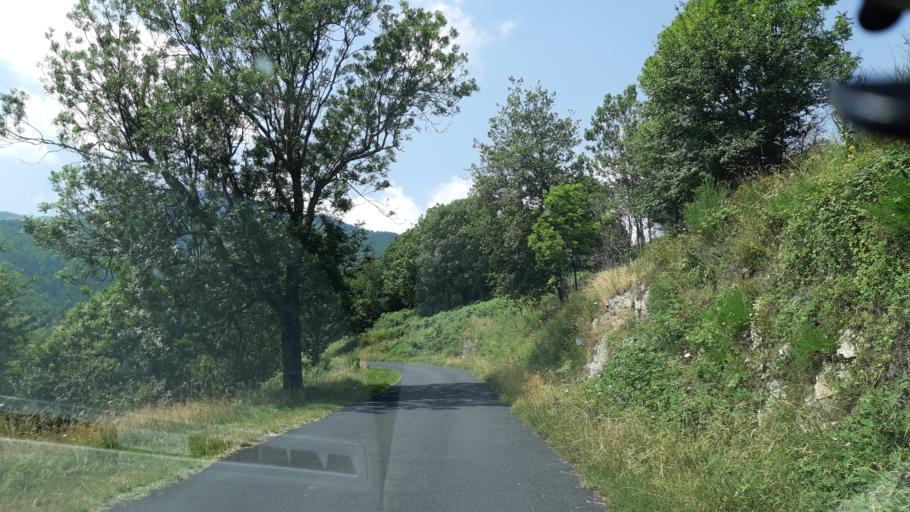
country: FR
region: Languedoc-Roussillon
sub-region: Departement des Pyrenees-Orientales
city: Arles
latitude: 42.5384
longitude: 2.5689
